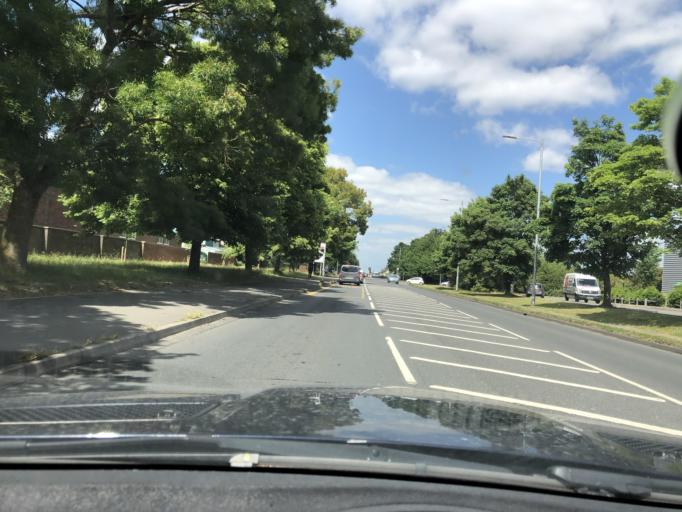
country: GB
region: England
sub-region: Essex
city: Chelmsford
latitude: 51.7246
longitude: 0.4512
